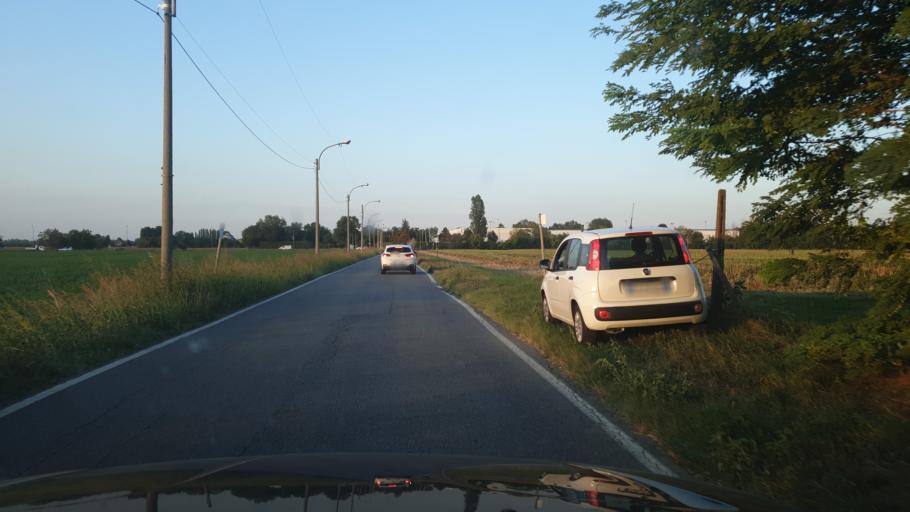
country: IT
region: Emilia-Romagna
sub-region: Provincia di Bologna
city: Quarto Inferiore
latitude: 44.5271
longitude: 11.3818
